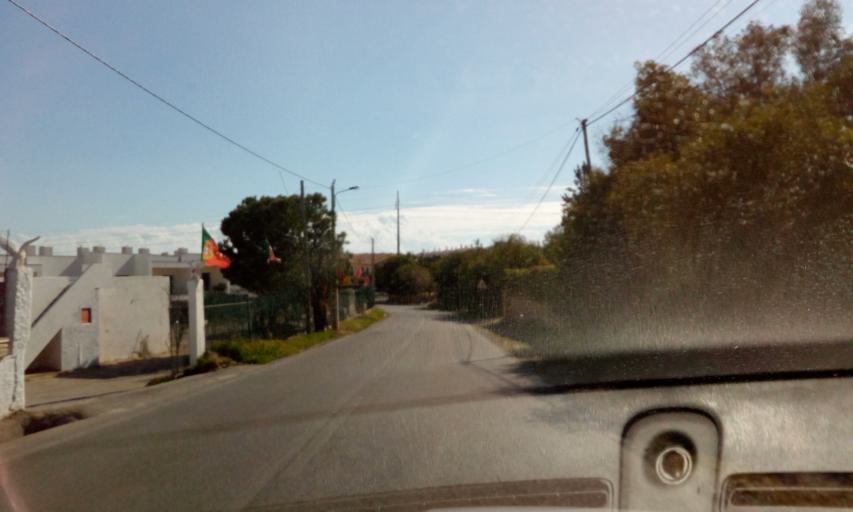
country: PT
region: Faro
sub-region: Albufeira
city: Ferreiras
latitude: 37.1147
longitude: -8.2127
